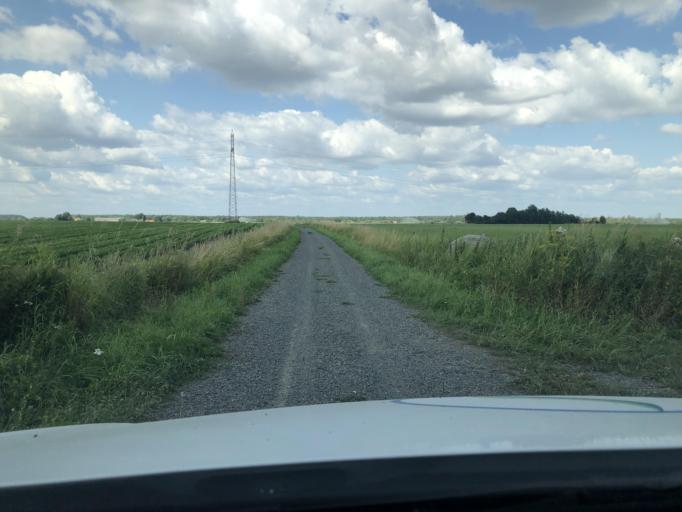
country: SE
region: Skane
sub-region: Kristianstads Kommun
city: Degeberga
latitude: 55.8835
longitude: 14.0818
